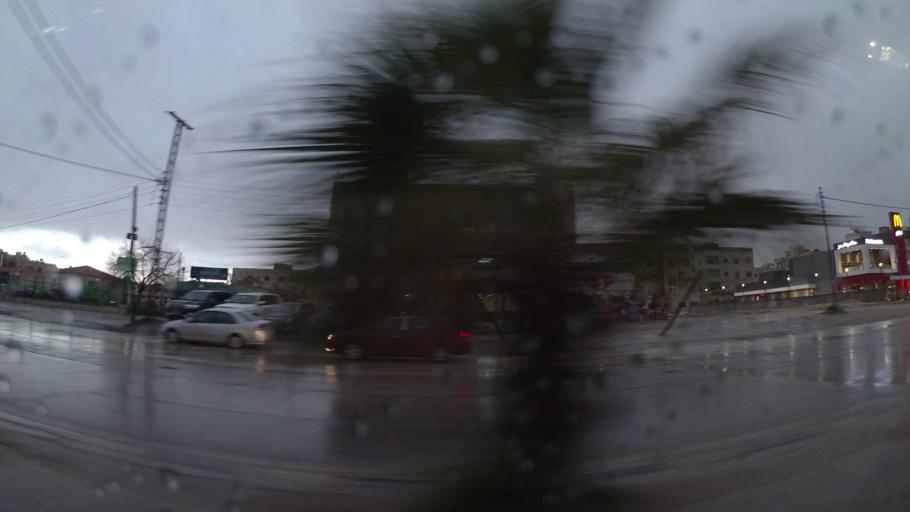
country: JO
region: Amman
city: Amman
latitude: 31.9886
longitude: 35.9470
